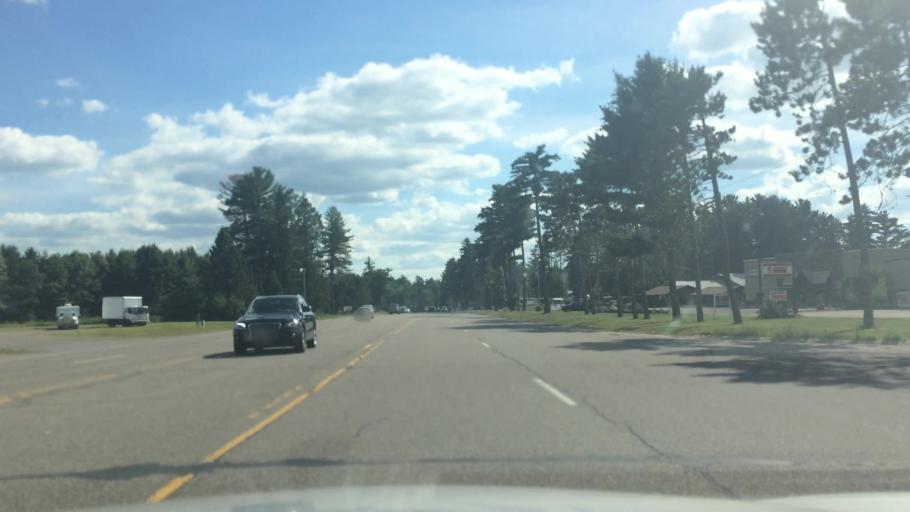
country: US
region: Wisconsin
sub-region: Vilas County
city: Lac du Flambeau
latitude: 45.8245
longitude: -89.7225
